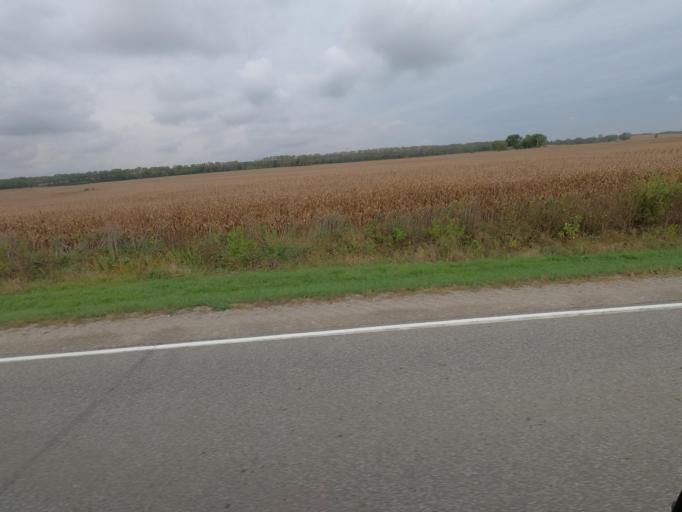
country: US
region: Iowa
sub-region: Wapello County
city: Ottumwa
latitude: 40.9087
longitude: -92.2081
